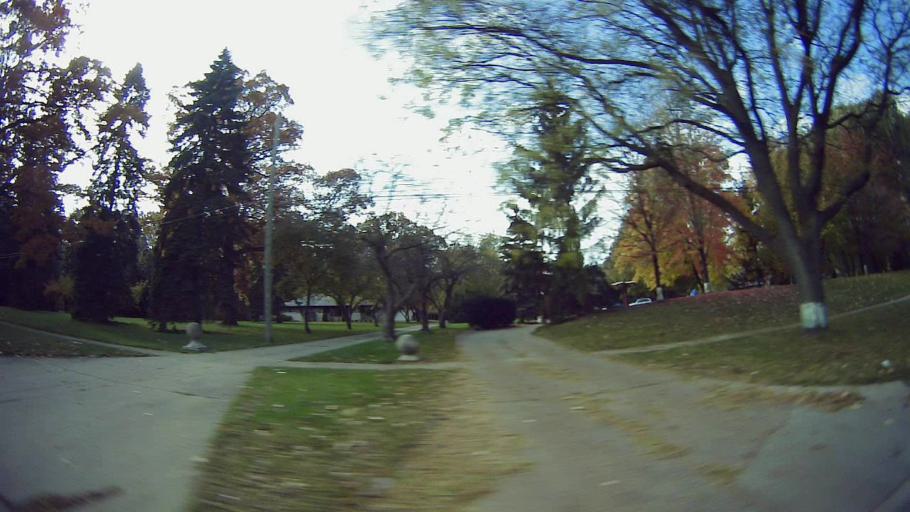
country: US
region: Michigan
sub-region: Macomb County
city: Center Line
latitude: 42.4818
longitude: -83.0663
